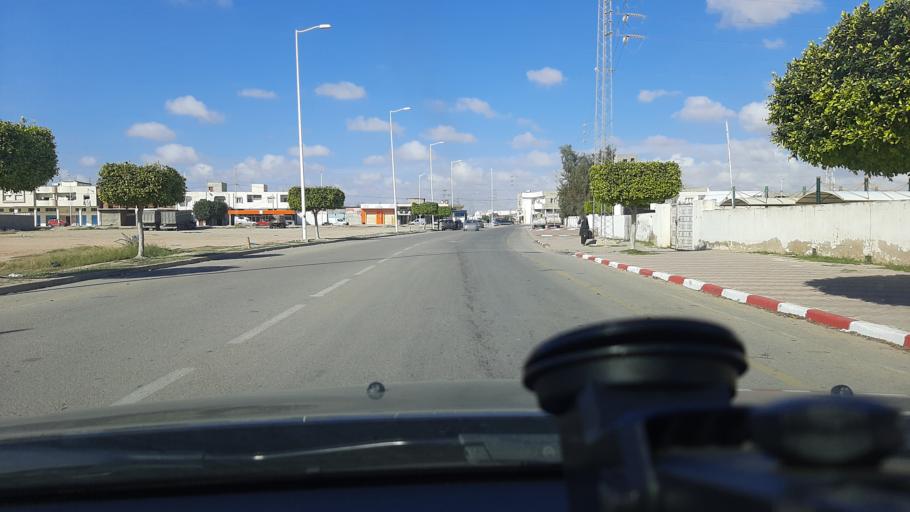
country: TN
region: Safaqis
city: Sfax
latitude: 34.8103
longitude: 10.7107
